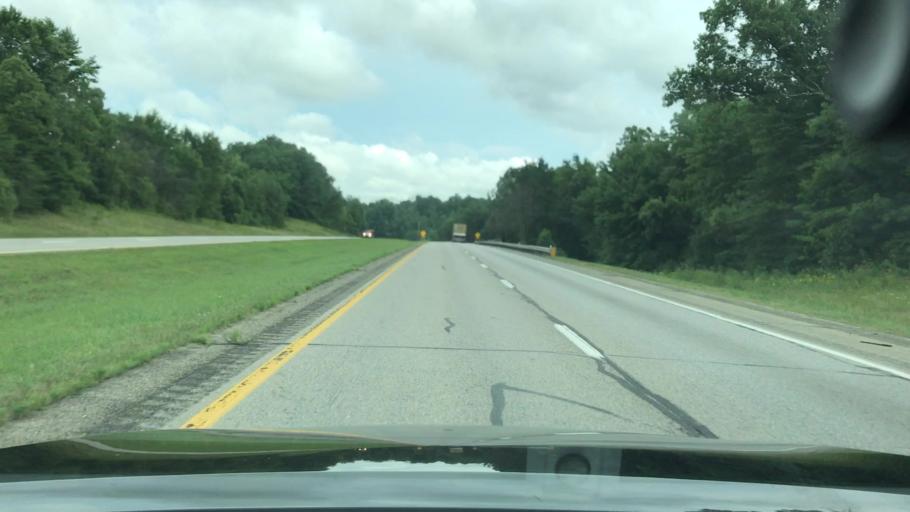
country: US
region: Ohio
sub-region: Jackson County
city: Oak Hill
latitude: 38.9799
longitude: -82.5251
